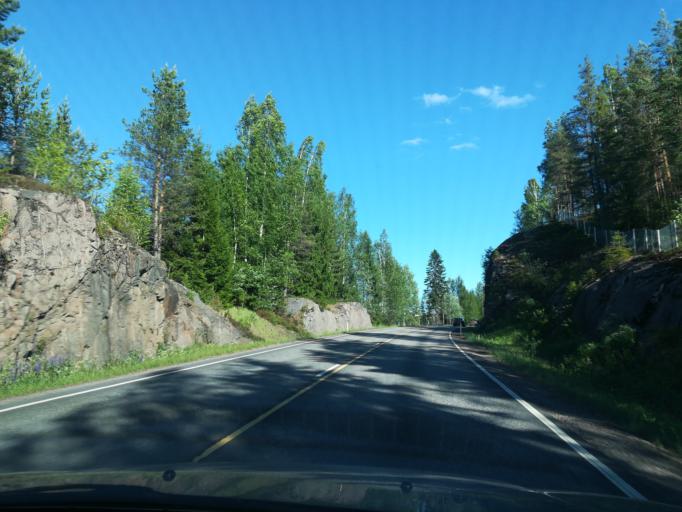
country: FI
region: South Karelia
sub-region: Imatra
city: Ruokolahti
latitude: 61.3635
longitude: 28.6965
